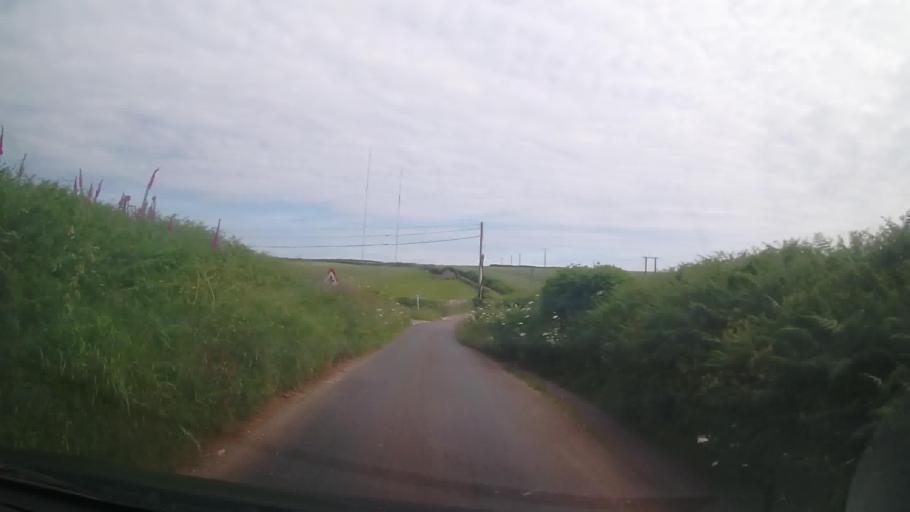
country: GB
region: England
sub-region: Devon
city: Salcombe
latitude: 50.2328
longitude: -3.6704
